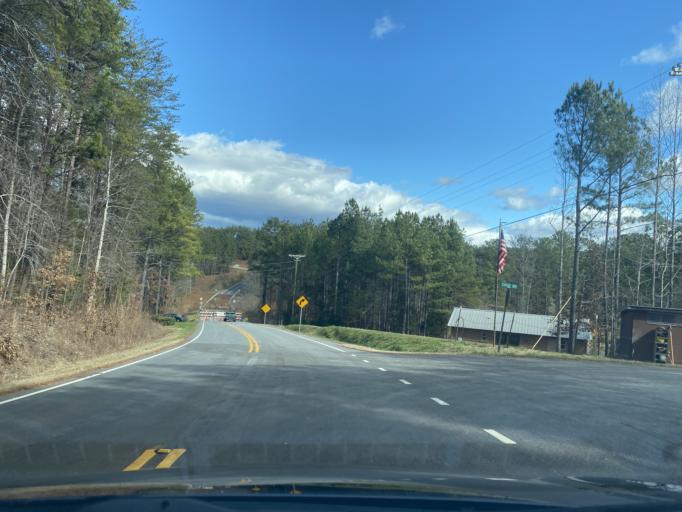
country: US
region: South Carolina
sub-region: Cherokee County
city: Gaffney
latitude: 35.0931
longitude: -81.7395
